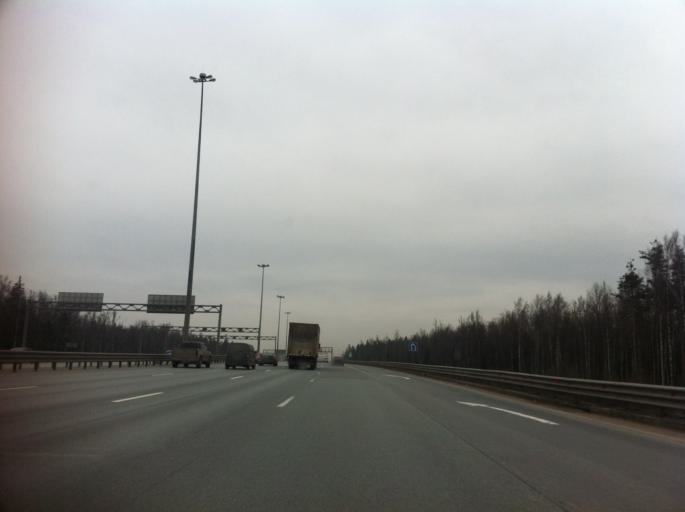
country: RU
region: St.-Petersburg
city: Krasnogvargeisky
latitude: 59.9428
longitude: 30.5394
